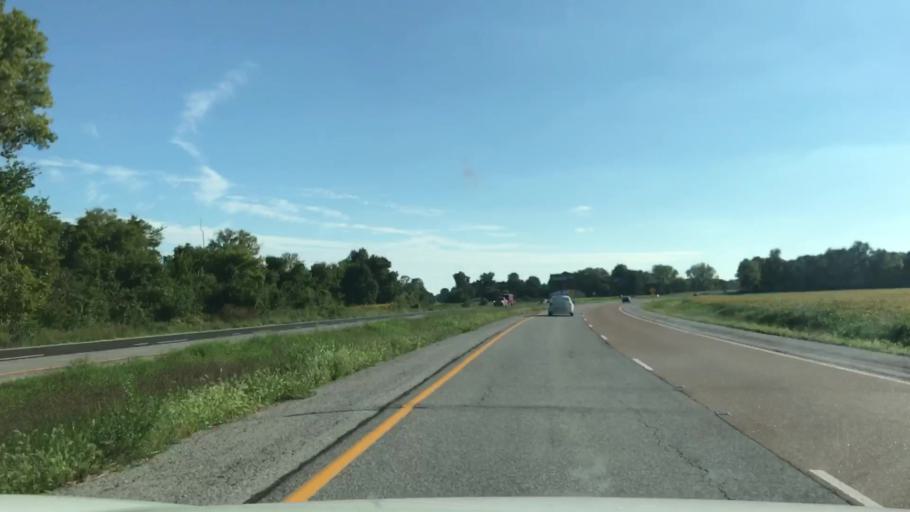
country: US
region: Illinois
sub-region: Madison County
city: Mitchell
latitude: 38.7824
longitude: -90.1087
